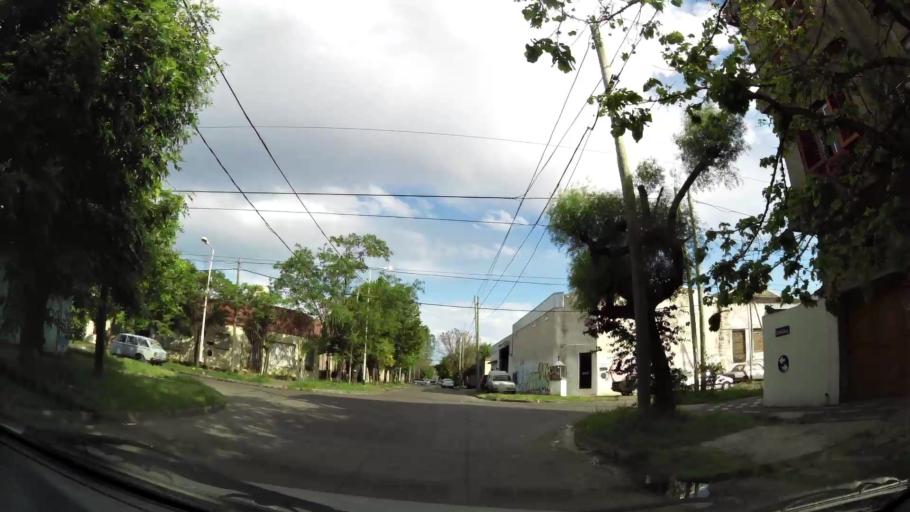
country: AR
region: Buenos Aires
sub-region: Partido de Lanus
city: Lanus
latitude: -34.6951
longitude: -58.3687
